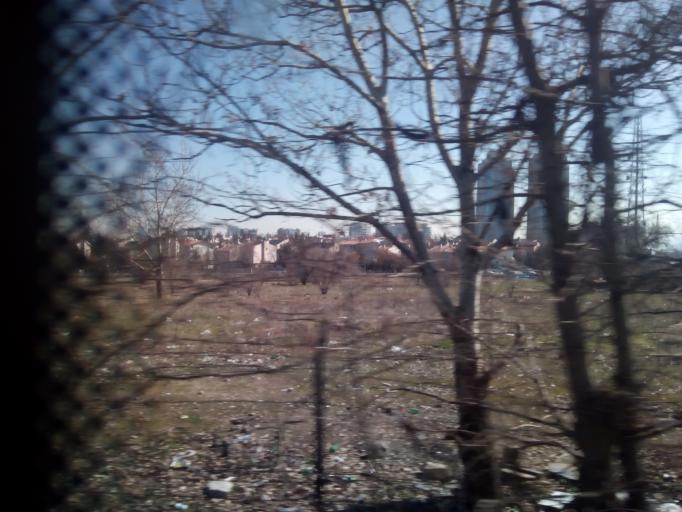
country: TR
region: Ankara
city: Batikent
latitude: 39.9110
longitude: 32.7546
